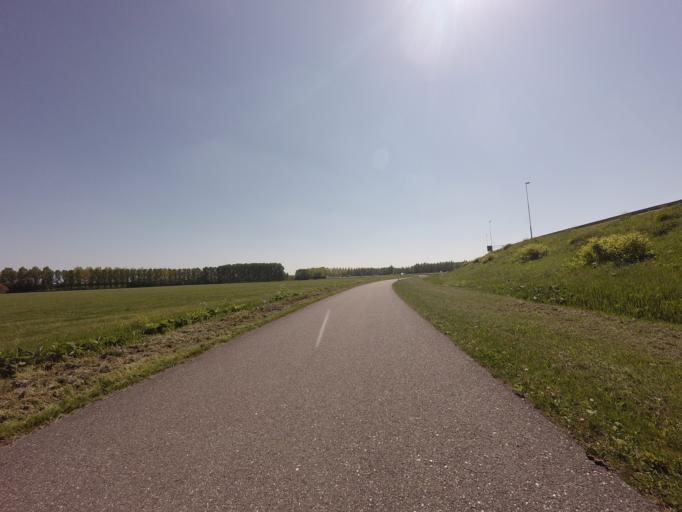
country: NL
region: South Holland
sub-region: Gemeente Strijen
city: Strijen
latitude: 51.7007
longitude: 4.6523
